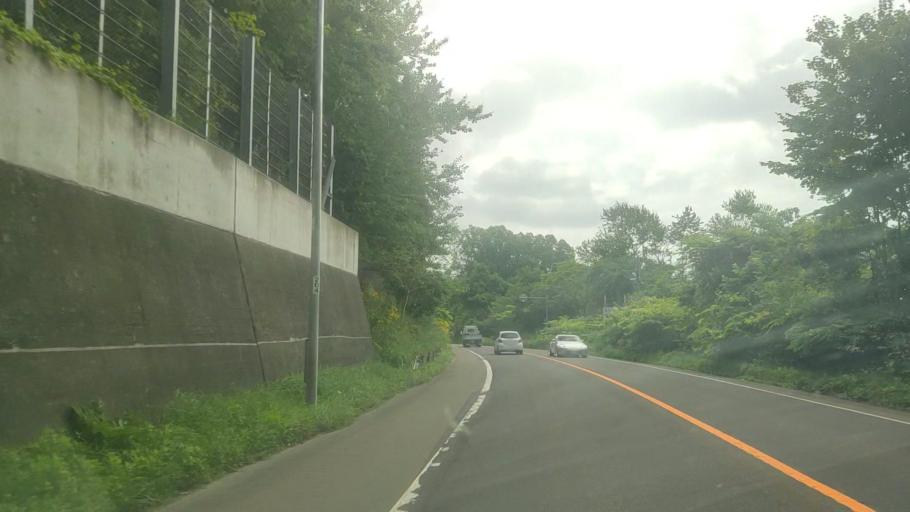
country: JP
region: Hokkaido
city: Niseko Town
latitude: 42.5915
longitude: 140.6752
